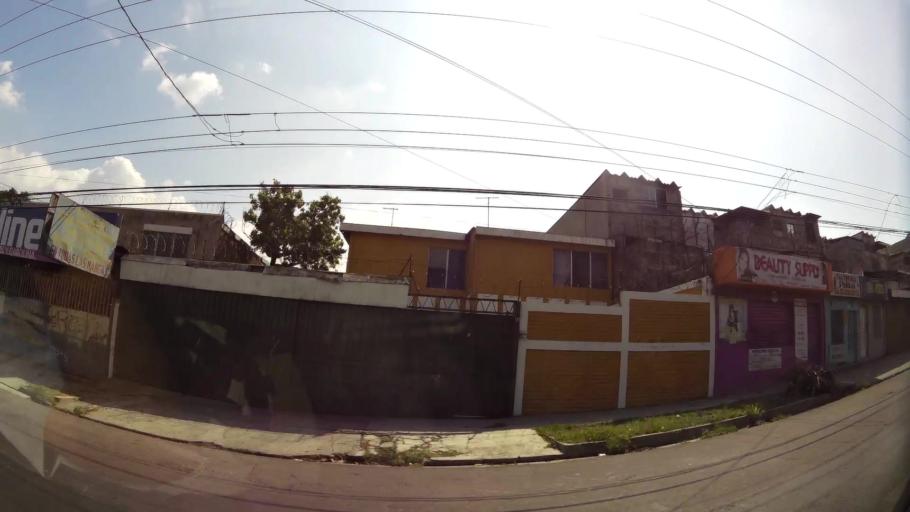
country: SV
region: San Salvador
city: Mejicanos
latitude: 13.7231
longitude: -89.2204
